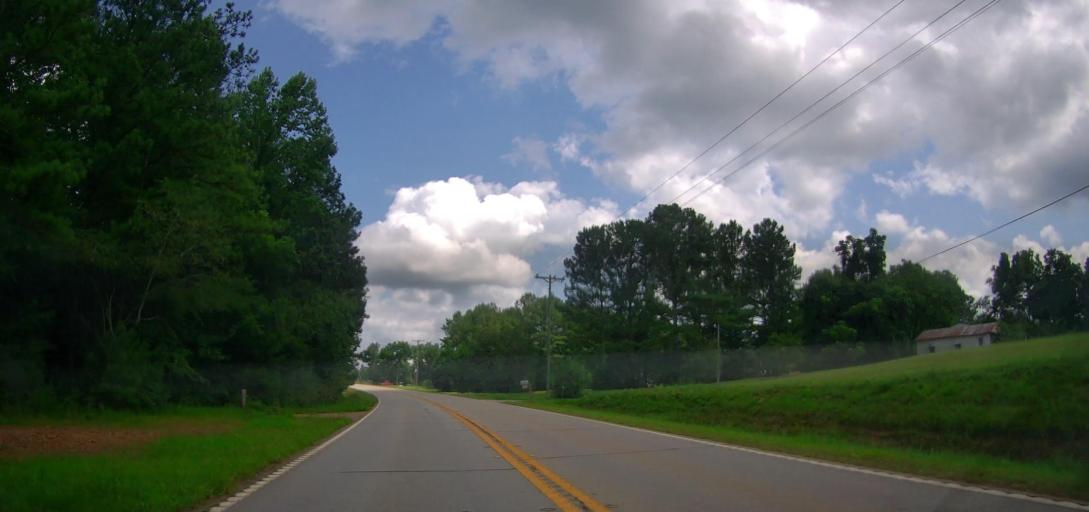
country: US
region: Georgia
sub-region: Heard County
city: Franklin
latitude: 33.3443
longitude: -85.1853
